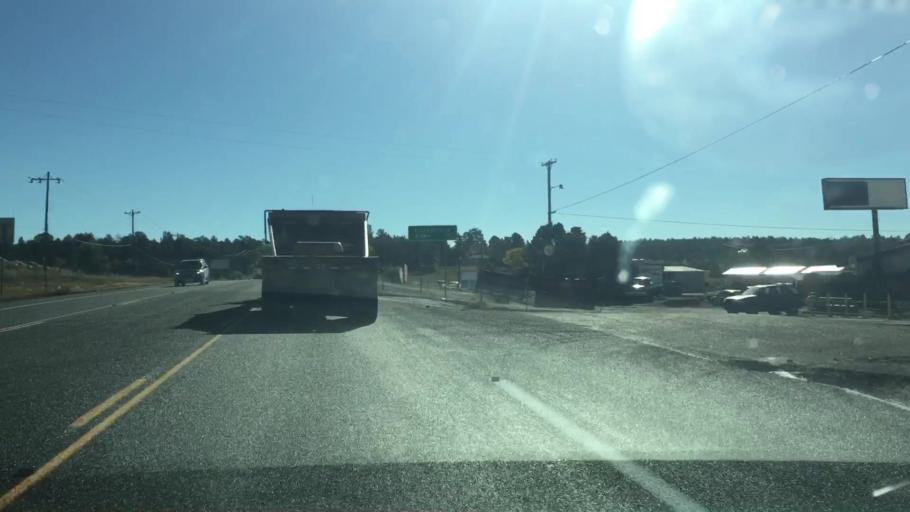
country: US
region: Colorado
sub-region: Douglas County
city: The Pinery
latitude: 39.3906
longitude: -104.7507
